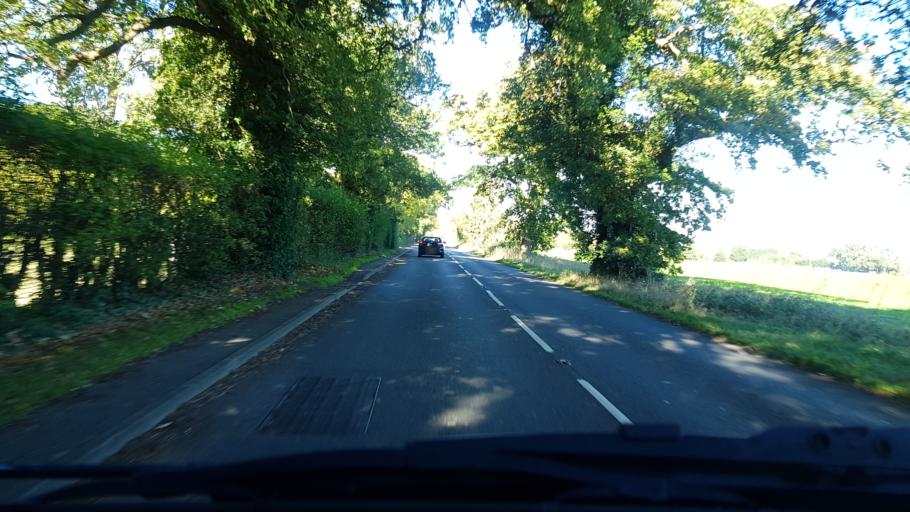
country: GB
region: England
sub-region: Surrey
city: Send
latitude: 51.2745
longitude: -0.5081
